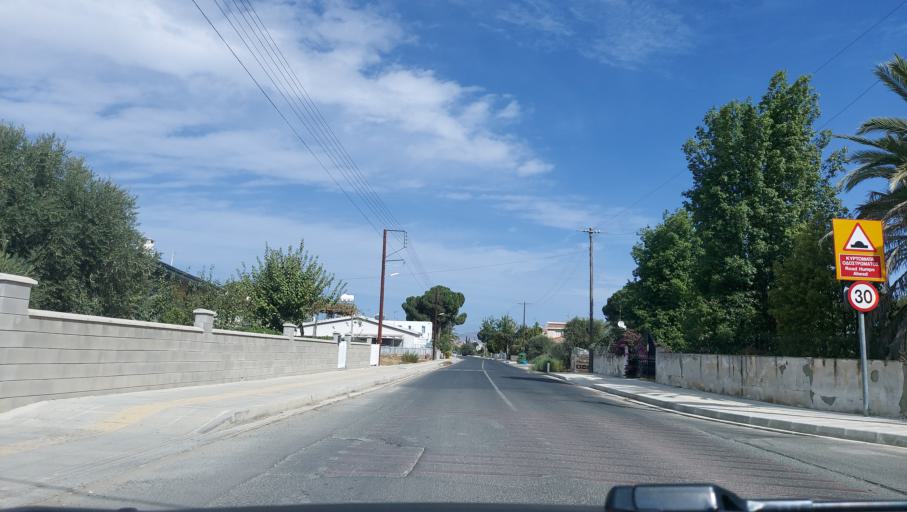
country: CY
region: Lefkosia
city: Pano Deftera
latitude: 35.0743
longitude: 33.2625
